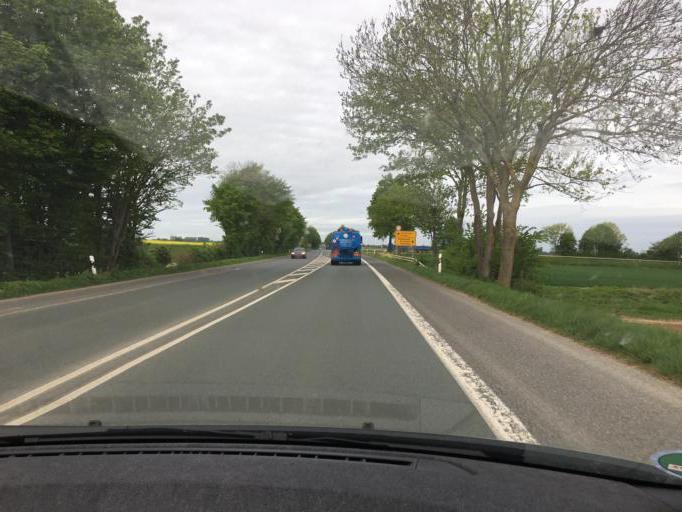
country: DE
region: North Rhine-Westphalia
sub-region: Regierungsbezirk Koln
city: Titz
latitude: 51.0427
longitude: 6.4333
